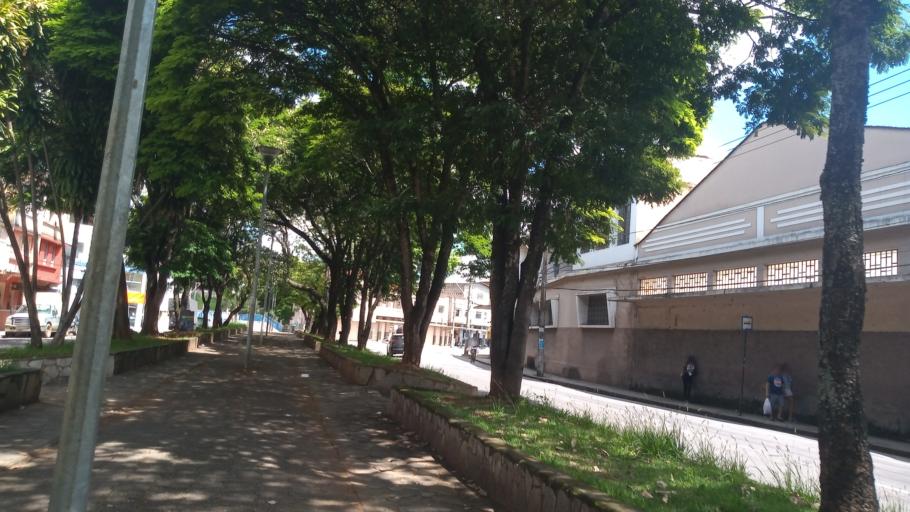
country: BR
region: Minas Gerais
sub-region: Sao Joao Del Rei
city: Sao Joao del Rei
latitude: -21.1294
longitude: -44.2504
